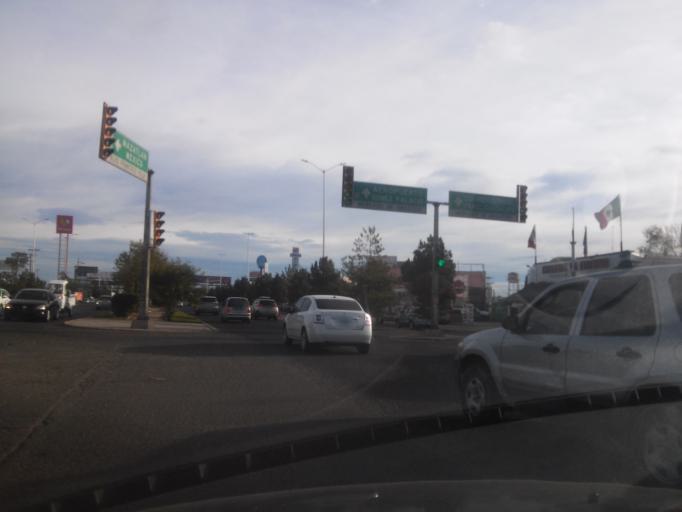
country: MX
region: Durango
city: Victoria de Durango
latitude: 24.0400
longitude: -104.6313
